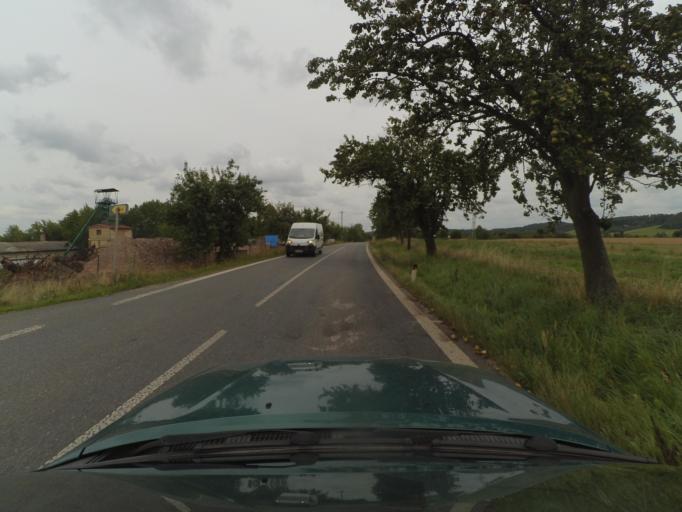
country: CZ
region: Central Bohemia
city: Rakovnik
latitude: 50.0788
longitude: 13.7122
